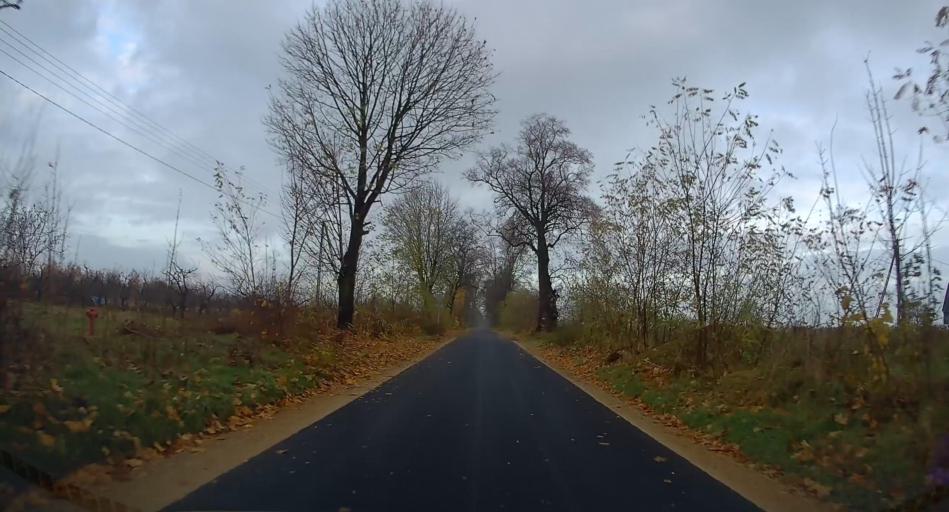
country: PL
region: Lodz Voivodeship
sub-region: Powiat skierniewicki
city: Kowiesy
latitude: 51.9225
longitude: 20.4117
